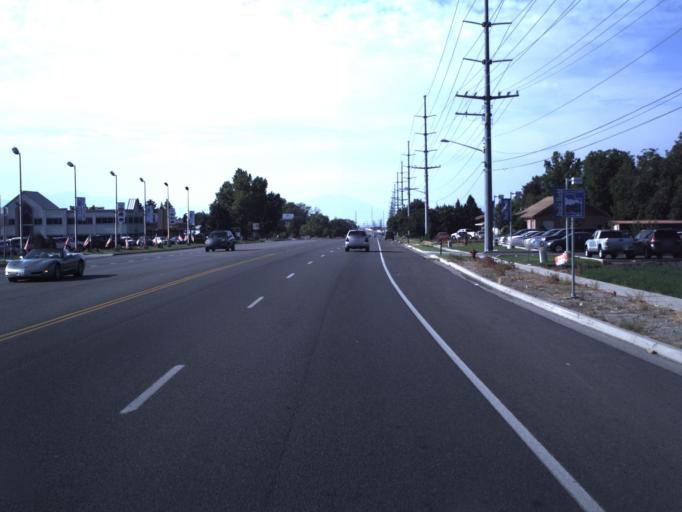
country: US
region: Utah
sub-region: Utah County
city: American Fork
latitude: 40.3724
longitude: -111.7854
